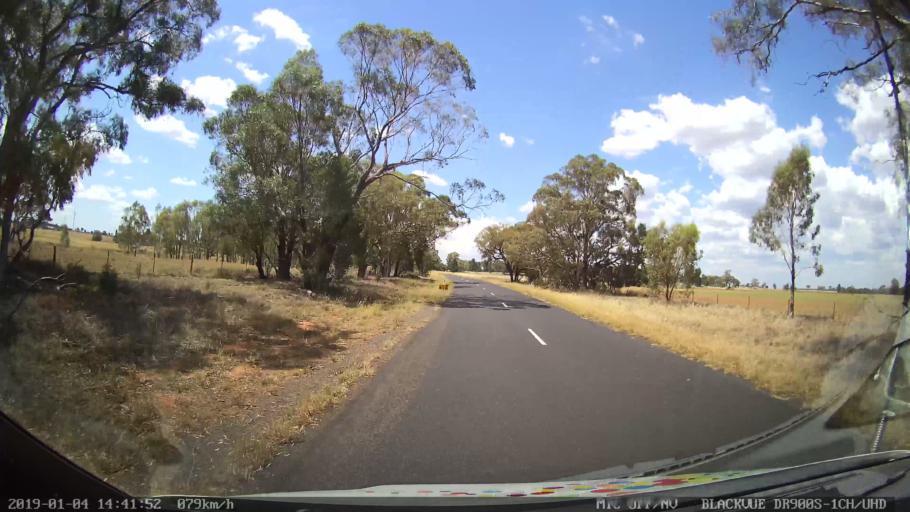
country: AU
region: New South Wales
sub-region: Dubbo Municipality
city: Dubbo
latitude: -32.1345
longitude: 148.6388
